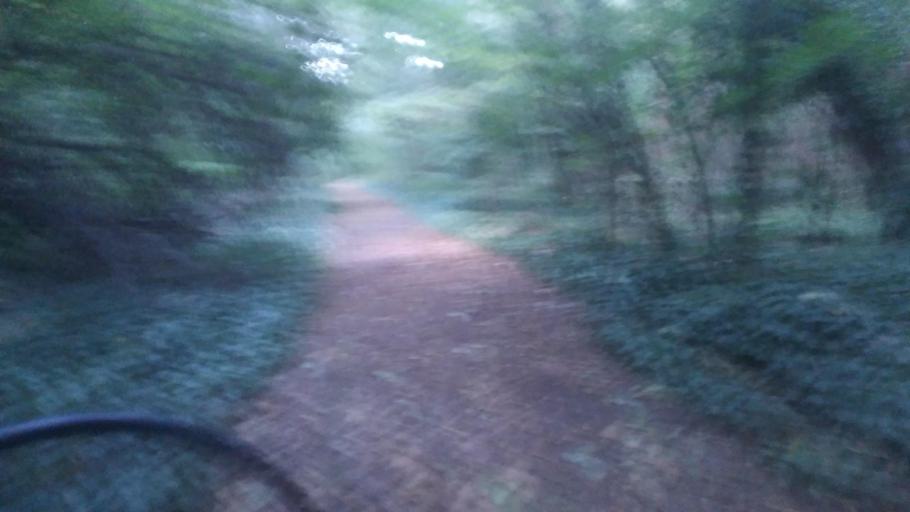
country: HU
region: Budapest
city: Budapest XVIII. keruelet
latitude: 47.4745
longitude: 19.1953
